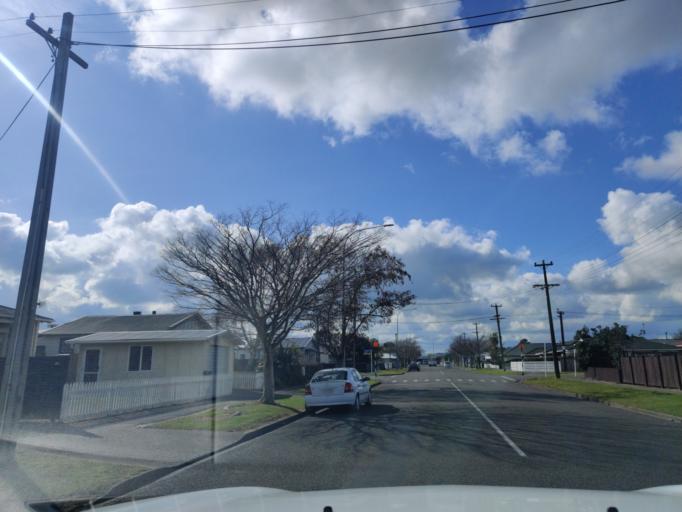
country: NZ
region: Manawatu-Wanganui
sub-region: Palmerston North City
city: Palmerston North
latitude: -40.3330
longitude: 175.6130
